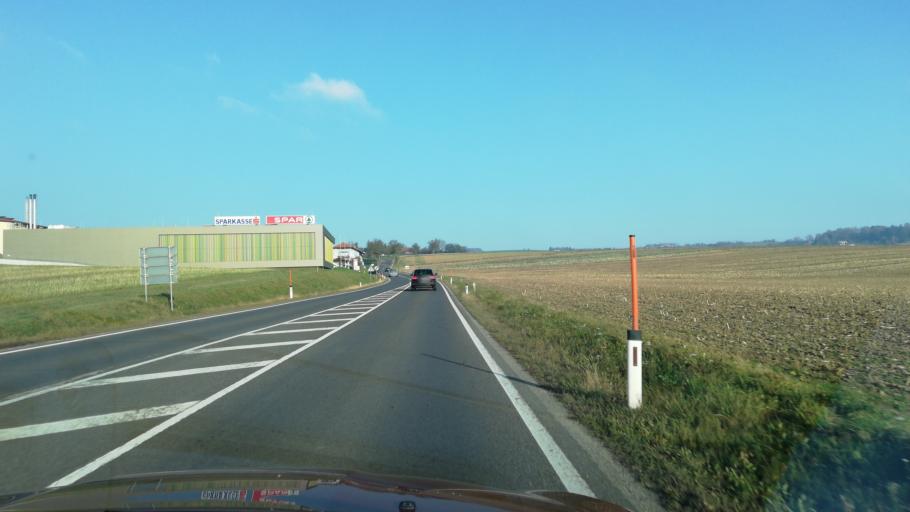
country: AT
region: Upper Austria
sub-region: Wels-Land
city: Buchkirchen
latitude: 48.2239
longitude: 14.0292
